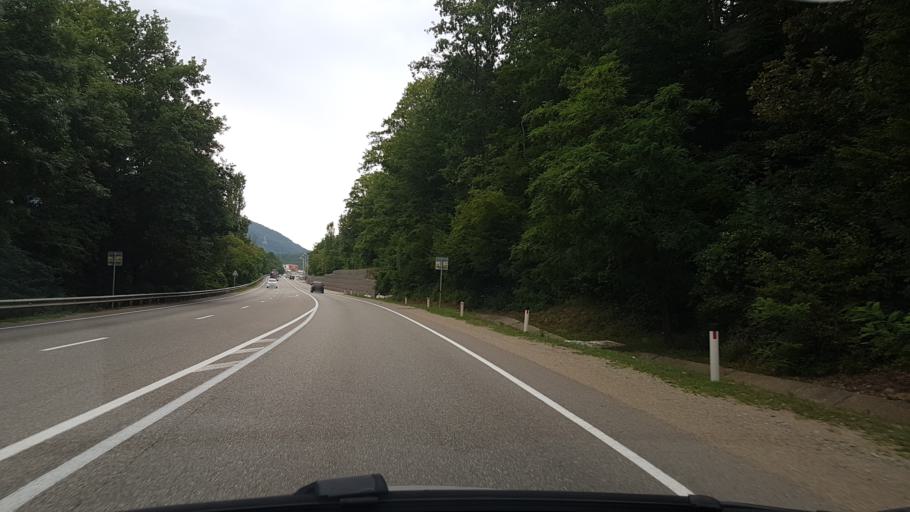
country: RU
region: Krasnodarskiy
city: Novomikhaylovskiy
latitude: 44.4724
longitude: 38.8868
